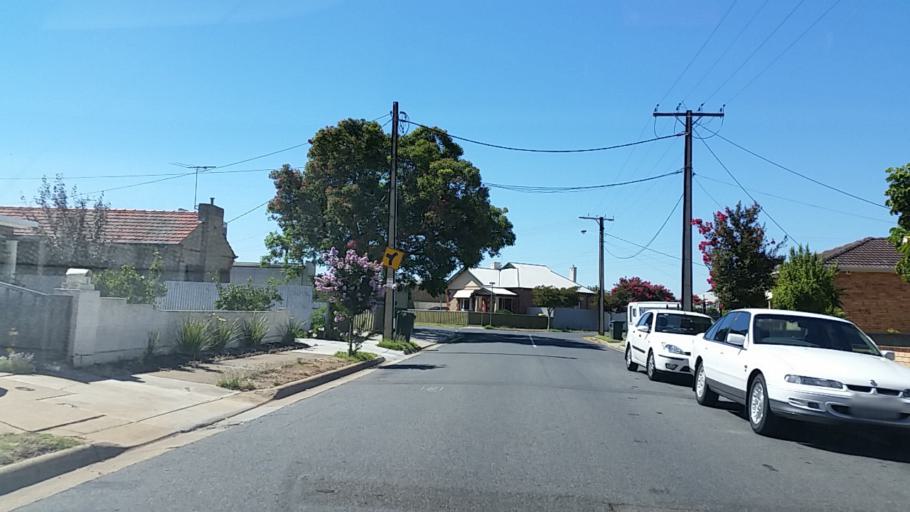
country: AU
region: South Australia
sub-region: Port Adelaide Enfield
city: Cheltenham
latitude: -34.8694
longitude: 138.5156
